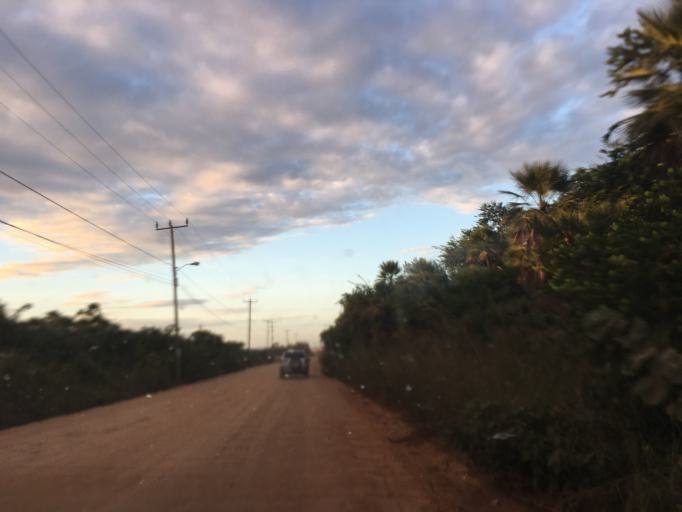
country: BZ
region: Stann Creek
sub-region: Dangriga
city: Dangriga
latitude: 16.8444
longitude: -88.2766
